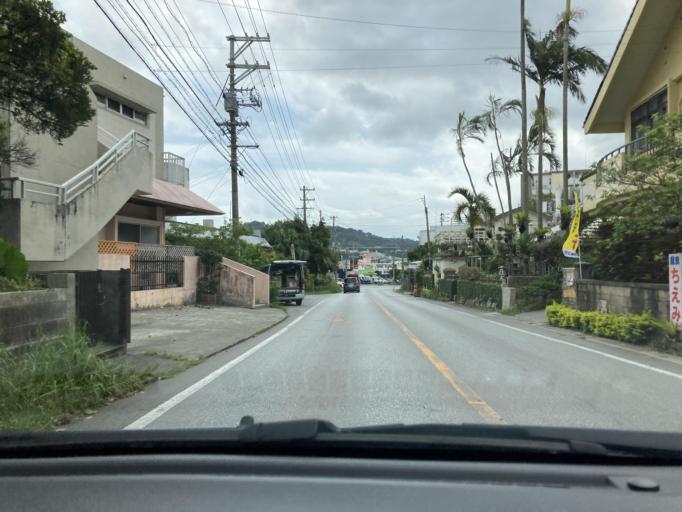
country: JP
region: Okinawa
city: Chatan
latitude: 26.2871
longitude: 127.7865
